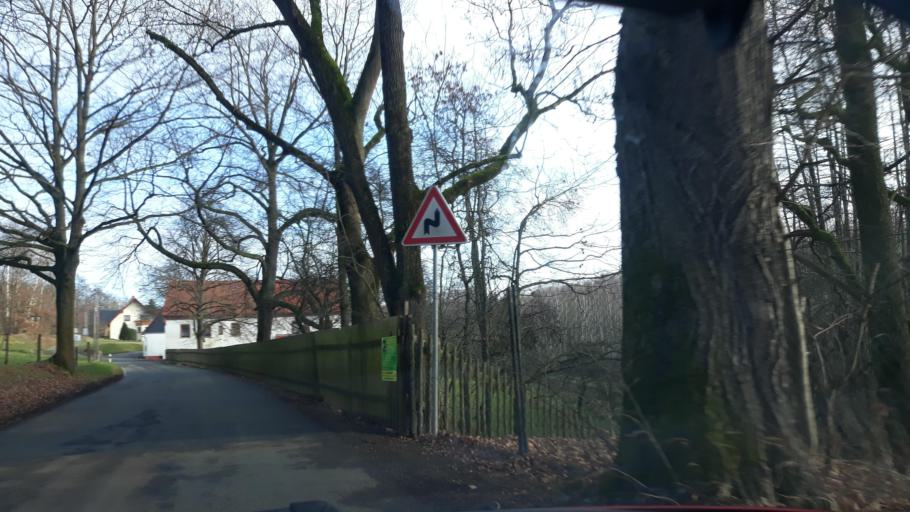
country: DE
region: Saxony
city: Zwickau
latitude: 50.7153
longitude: 12.5243
